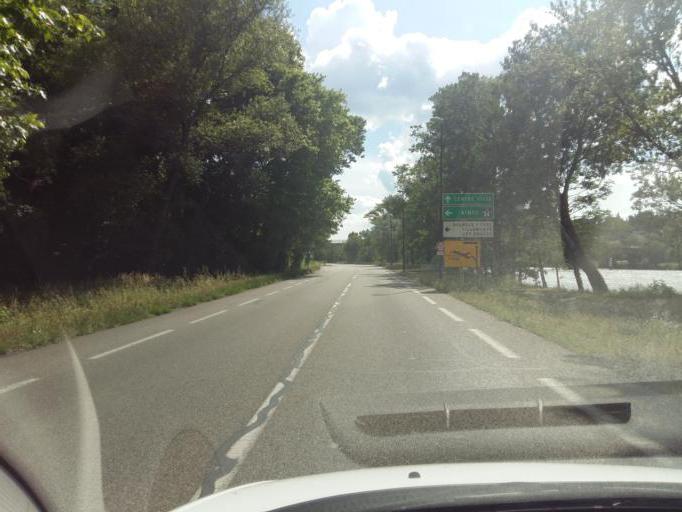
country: FR
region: Languedoc-Roussillon
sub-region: Departement du Gard
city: Villeneuve-les-Avignon
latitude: 43.9547
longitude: 4.7964
